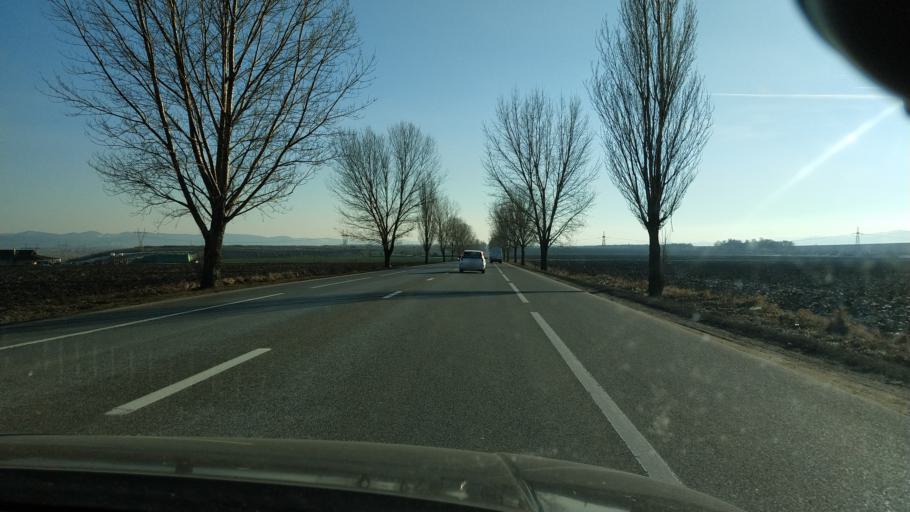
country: RO
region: Bacau
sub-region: Comuna Itesti
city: Itesti
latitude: 46.6529
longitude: 26.9077
